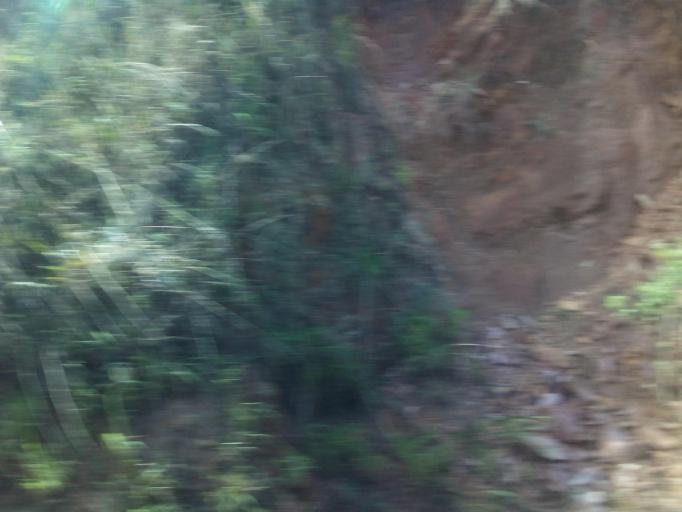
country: BR
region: Minas Gerais
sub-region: Raposos
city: Raposos
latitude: -19.8735
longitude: -43.7796
